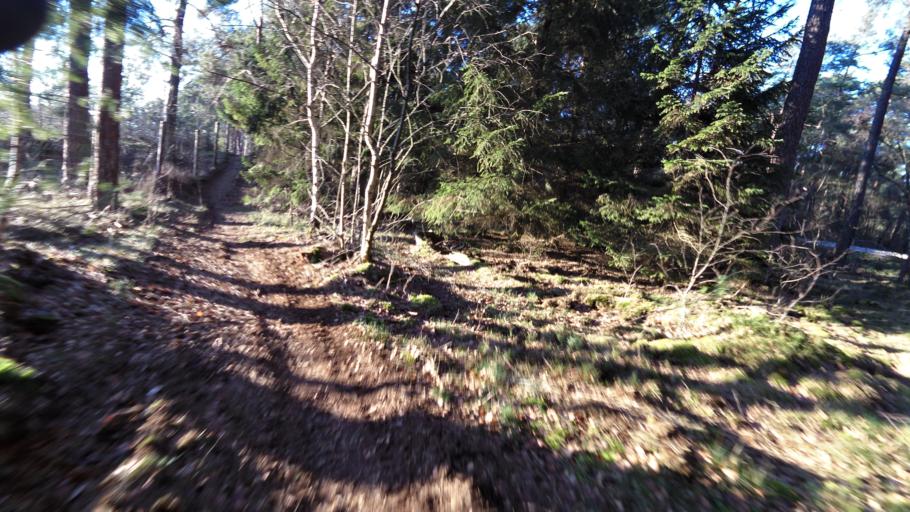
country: NL
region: Gelderland
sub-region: Gemeente Barneveld
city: Stroe
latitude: 52.1946
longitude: 5.7297
